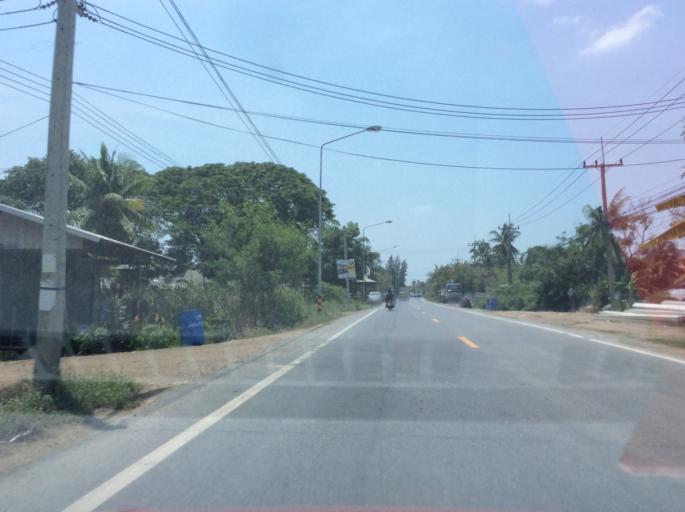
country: TH
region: Pathum Thani
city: Ban Rangsit
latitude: 14.0089
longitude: 100.7794
